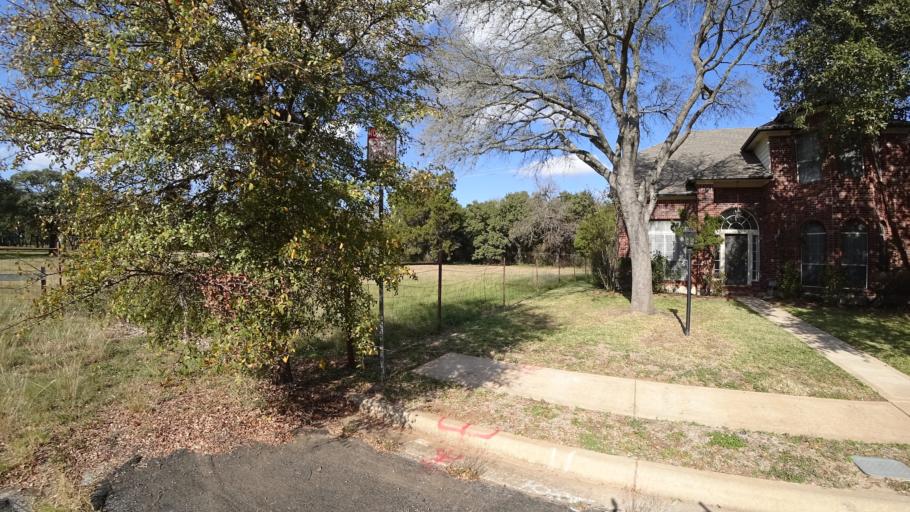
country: US
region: Texas
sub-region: Travis County
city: Shady Hollow
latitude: 30.1842
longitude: -97.8579
